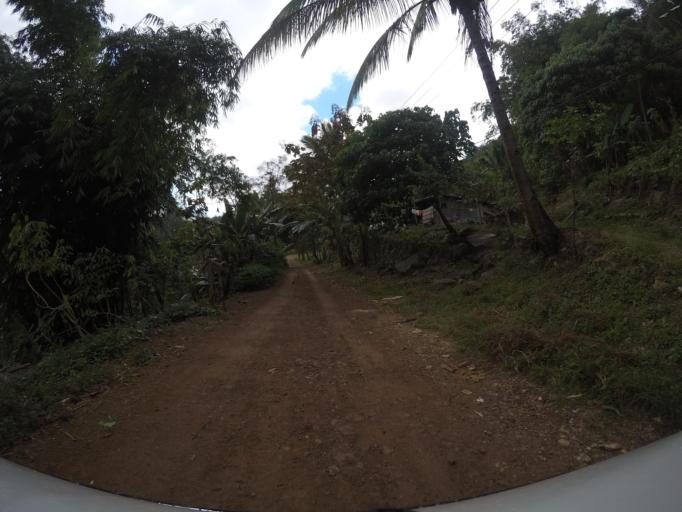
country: TL
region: Baucau
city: Baucau
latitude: -8.6484
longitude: 126.6268
